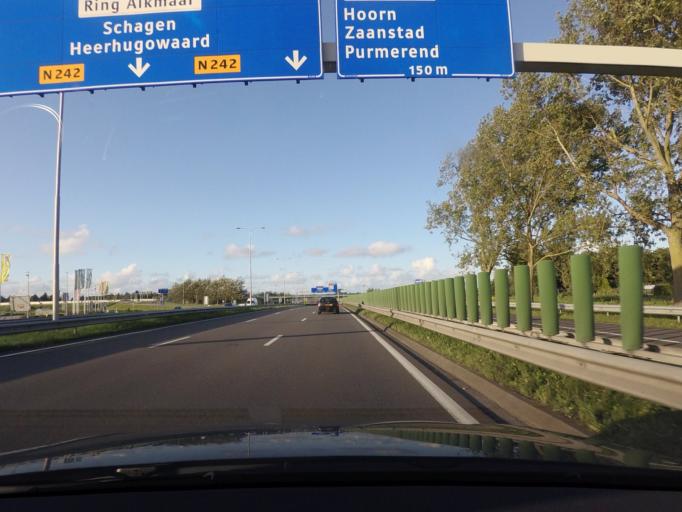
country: NL
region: North Holland
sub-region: Gemeente Alkmaar
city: Alkmaar
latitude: 52.6212
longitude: 4.7763
